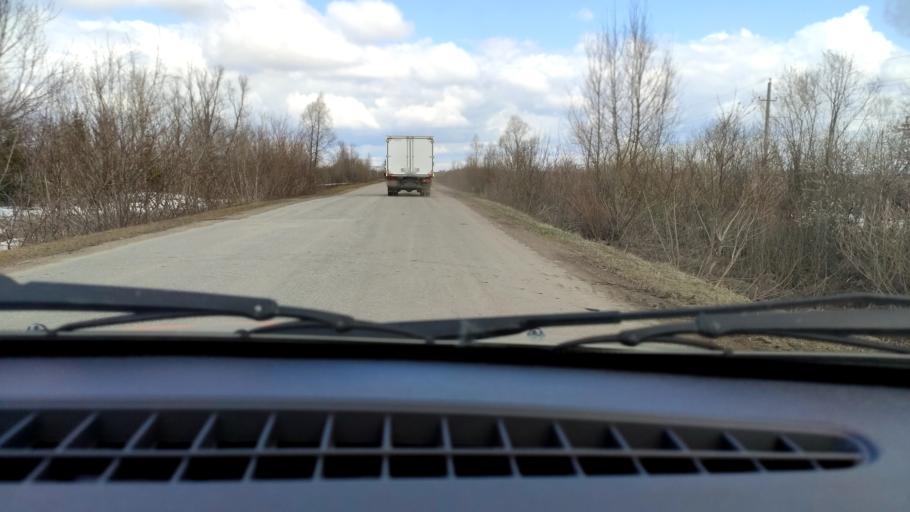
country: RU
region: Bashkortostan
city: Kudeyevskiy
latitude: 54.8320
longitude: 56.7929
